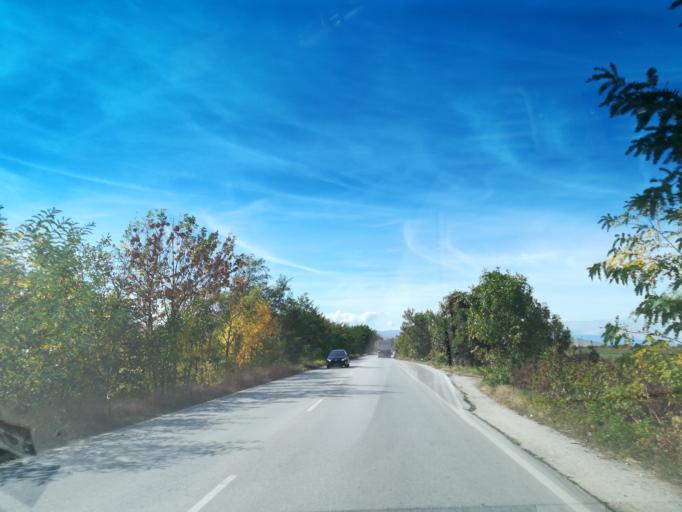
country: BG
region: Plovdiv
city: Stamboliyski
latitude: 42.1186
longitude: 24.5453
